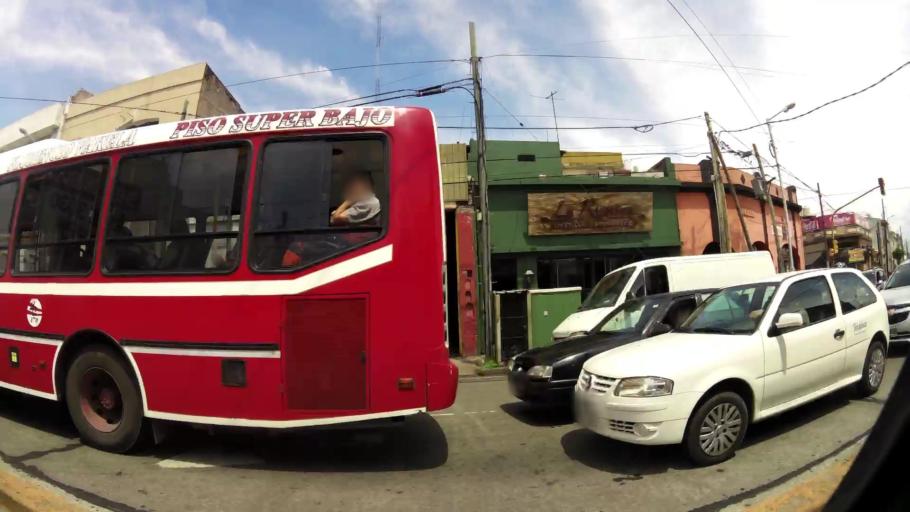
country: AR
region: Buenos Aires
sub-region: Partido de Avellaneda
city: Avellaneda
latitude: -34.6671
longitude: -58.3846
